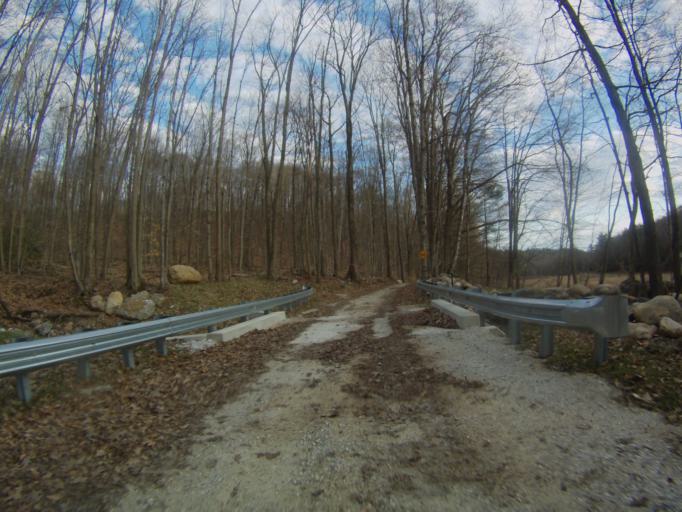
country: US
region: Vermont
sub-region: Rutland County
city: Brandon
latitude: 43.8420
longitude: -73.0415
